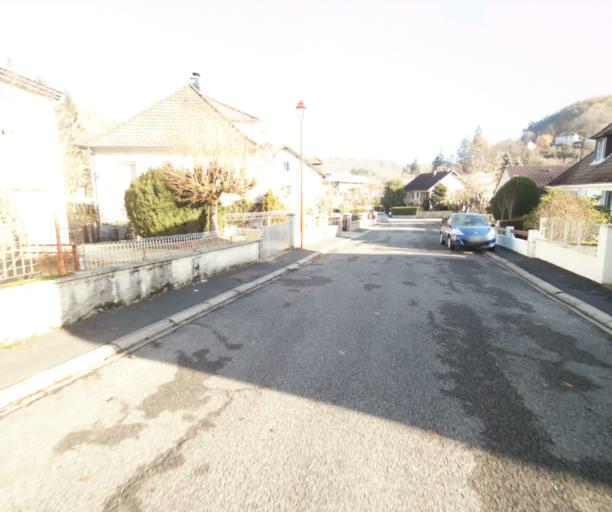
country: FR
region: Limousin
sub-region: Departement de la Correze
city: Laguenne
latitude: 45.2440
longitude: 1.7748
